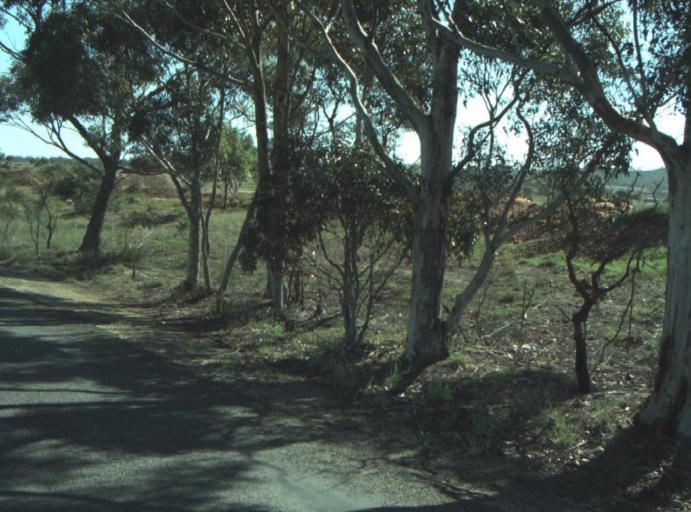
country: AU
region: Victoria
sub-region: Greater Geelong
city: Lara
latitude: -37.9316
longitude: 144.3944
